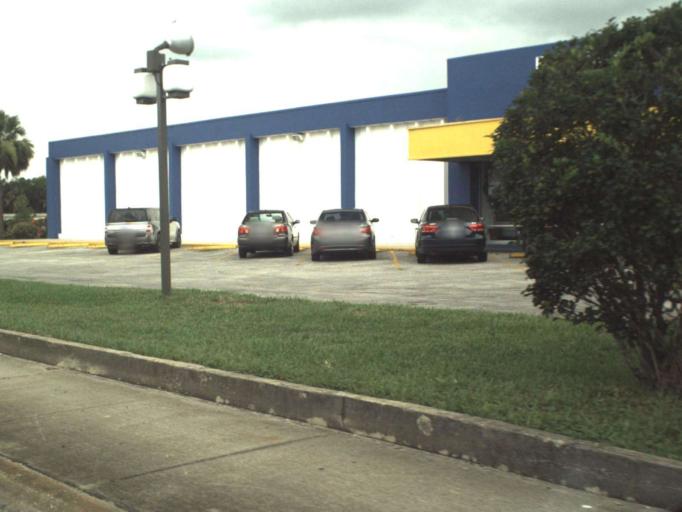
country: US
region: Florida
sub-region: Seminole County
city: Altamonte Springs
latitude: 28.6630
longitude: -81.3566
